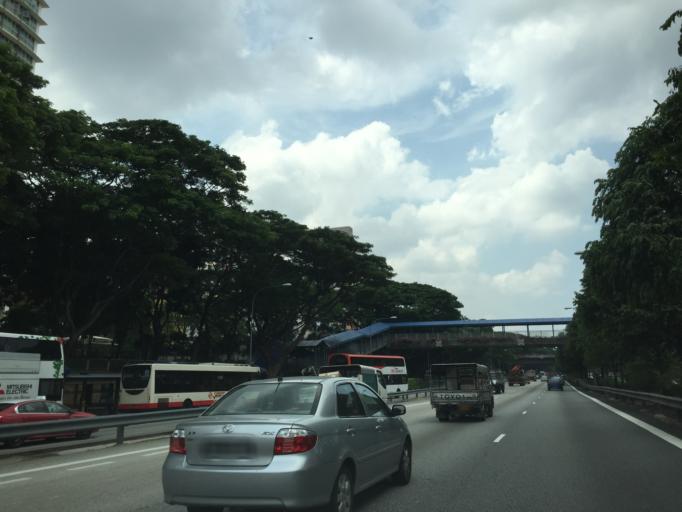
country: SG
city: Singapore
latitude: 1.3297
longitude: 103.8435
